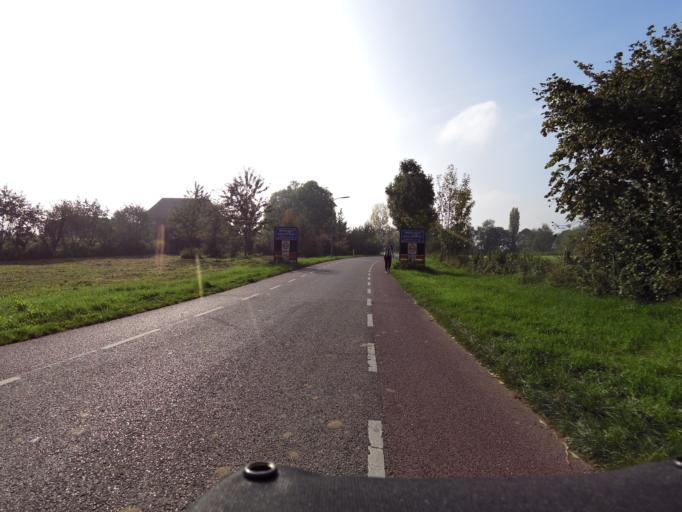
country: NL
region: Gelderland
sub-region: Gemeente Zevenaar
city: Zevenaar
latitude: 51.8595
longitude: 6.0408
